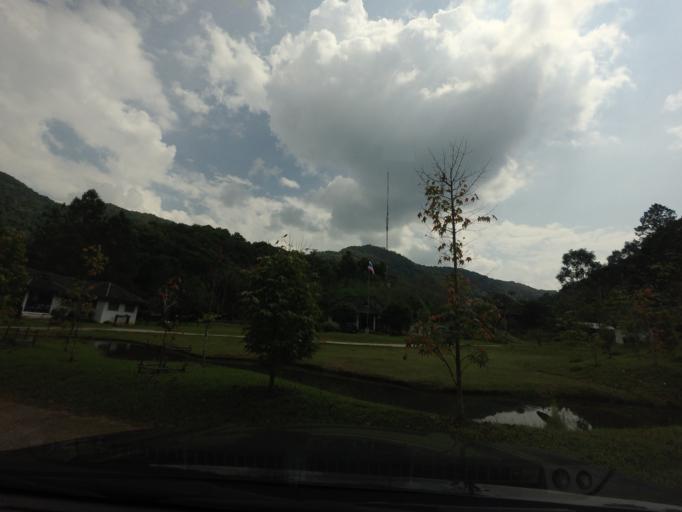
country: TH
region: Nan
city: Bo Kluea
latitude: 19.1811
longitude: 101.1792
